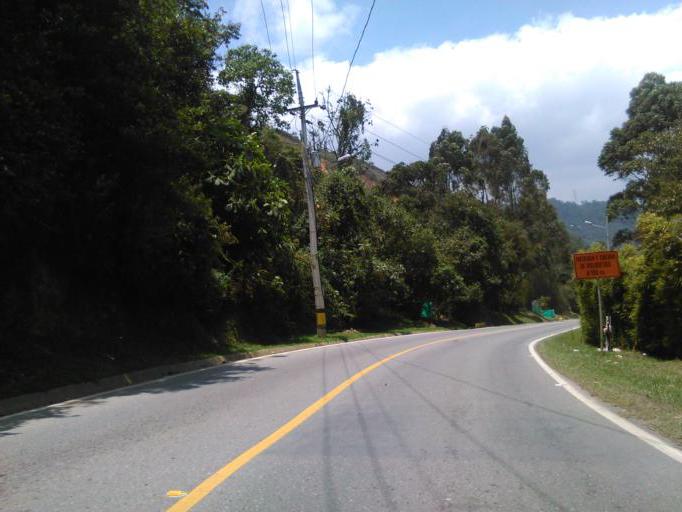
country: CO
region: Antioquia
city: La Union
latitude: 6.0024
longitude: -75.3835
